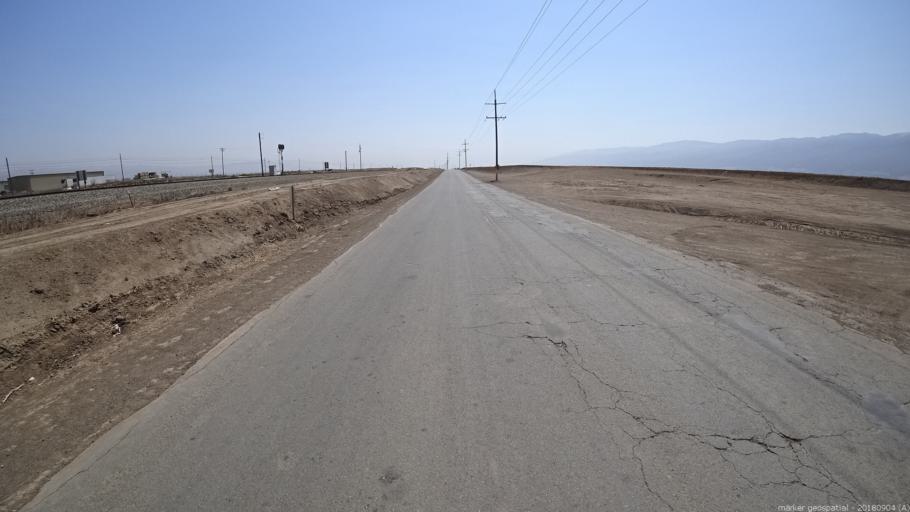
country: US
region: California
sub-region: Monterey County
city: Chualar
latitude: 36.5597
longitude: -121.5094
